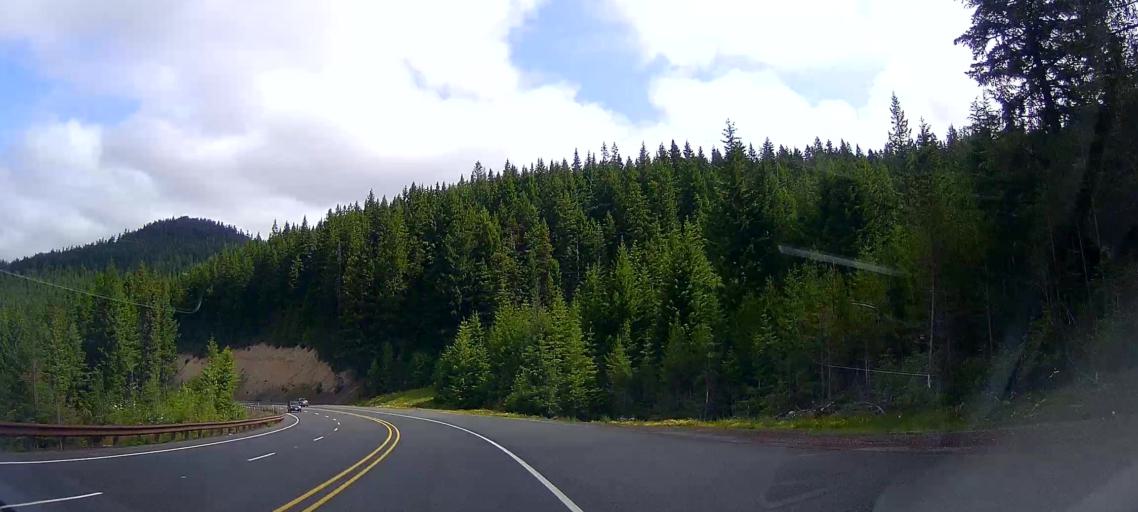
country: US
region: Oregon
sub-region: Clackamas County
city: Mount Hood Village
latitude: 45.2363
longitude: -121.6981
